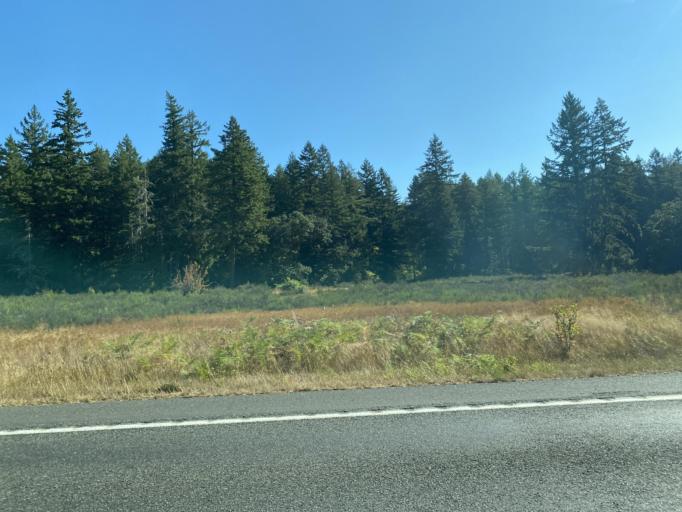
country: US
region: Washington
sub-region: Thurston County
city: Rainier
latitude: 46.9391
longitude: -122.7649
